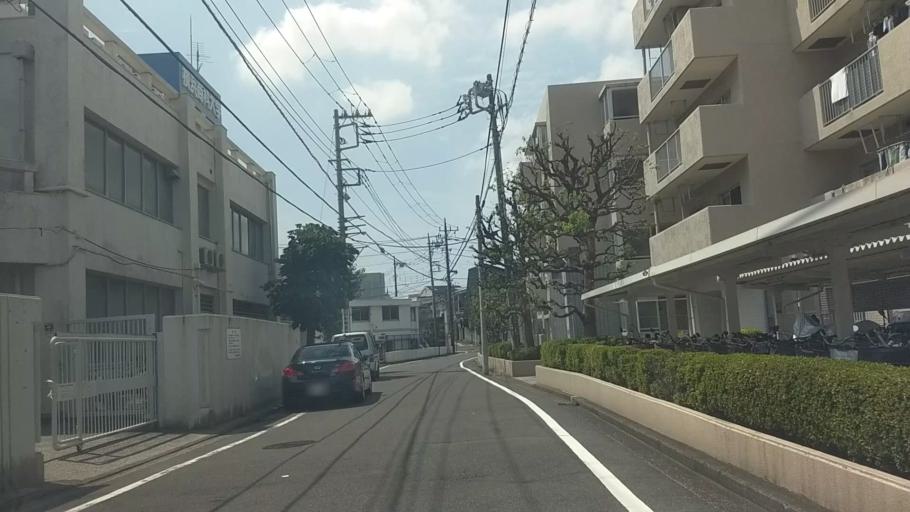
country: JP
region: Kanagawa
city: Yokohama
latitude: 35.4983
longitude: 139.6588
